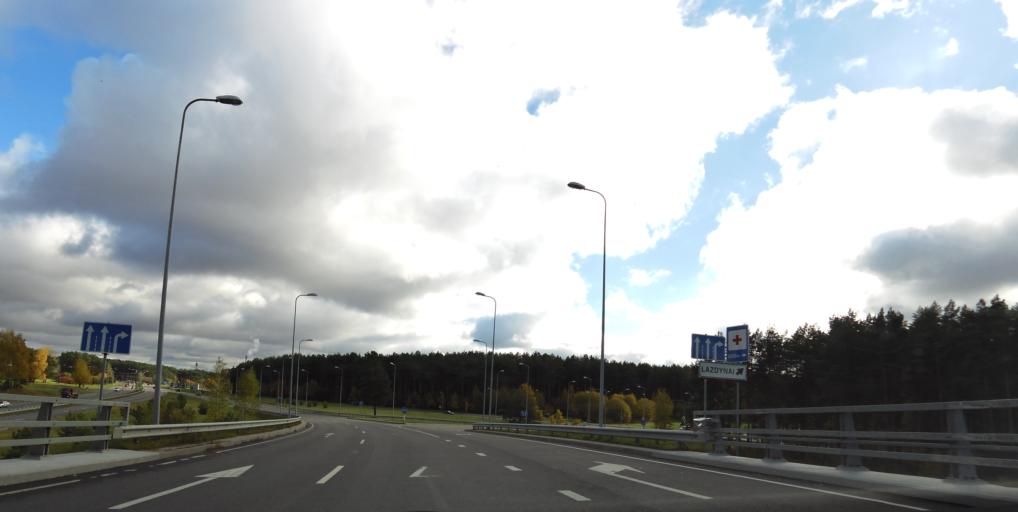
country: LT
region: Vilnius County
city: Lazdynai
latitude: 54.6713
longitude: 25.1973
